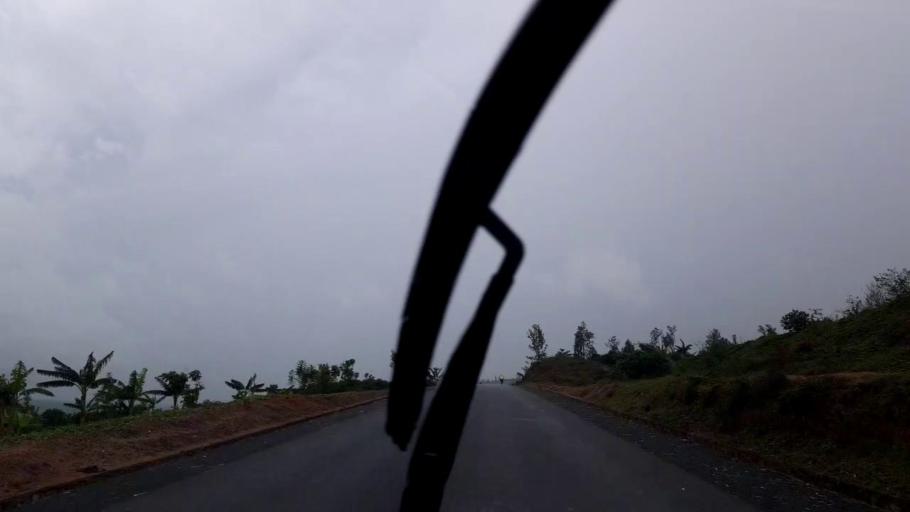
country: RW
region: Northern Province
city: Byumba
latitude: -1.4047
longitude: 30.2851
